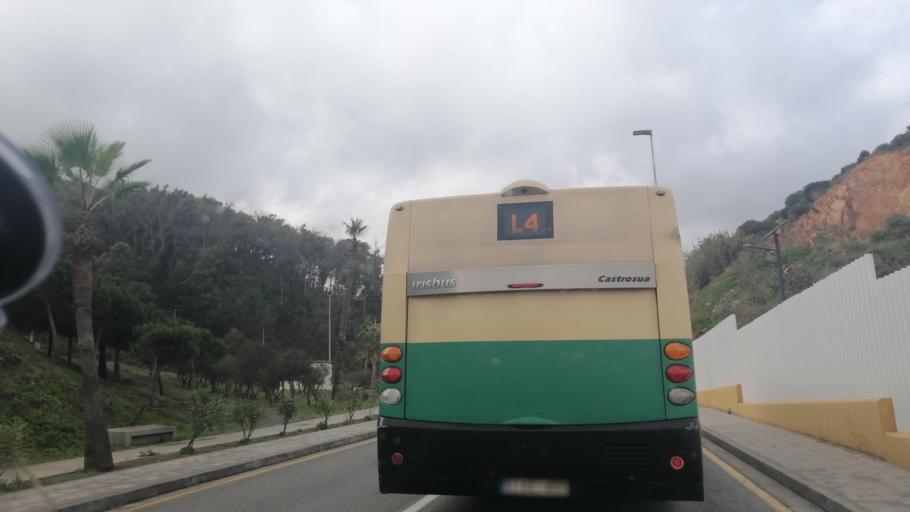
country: ES
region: Ceuta
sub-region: Ceuta
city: Ceuta
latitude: 35.8828
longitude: -5.3420
